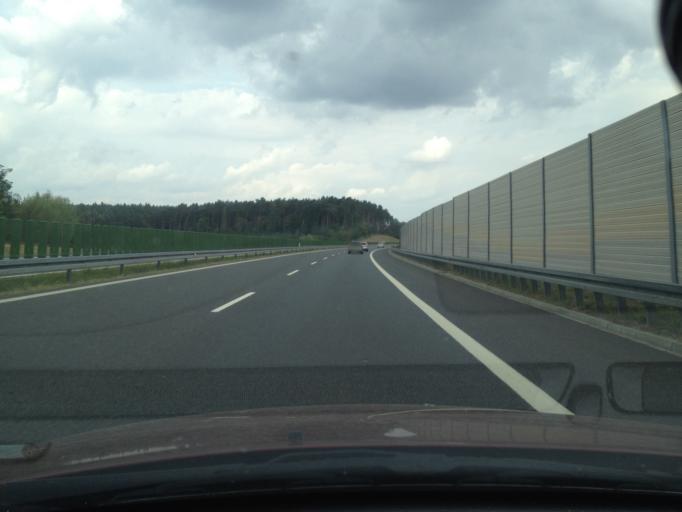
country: PL
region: West Pomeranian Voivodeship
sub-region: Powiat mysliborski
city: Mysliborz
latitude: 52.9949
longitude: 14.8632
